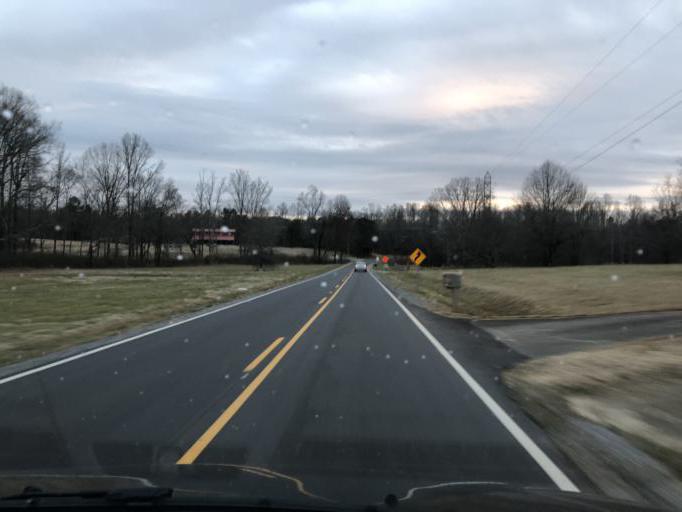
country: US
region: North Carolina
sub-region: Cleveland County
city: Shelby
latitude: 35.2509
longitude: -81.5238
